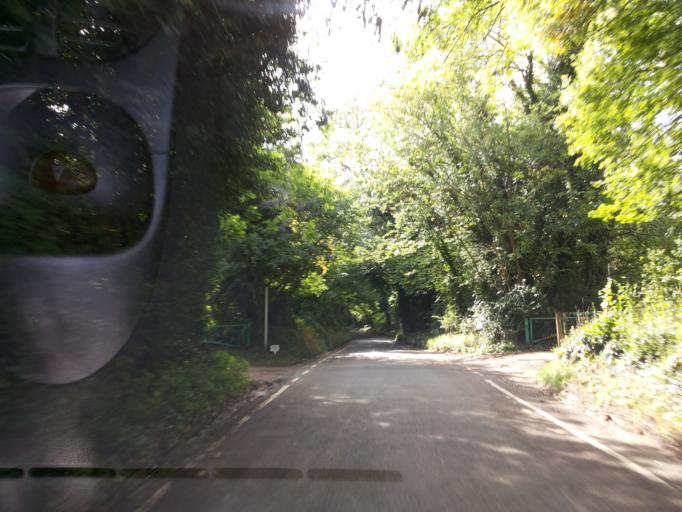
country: GB
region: England
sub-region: Greater London
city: Orpington
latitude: 51.3472
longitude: 0.0704
